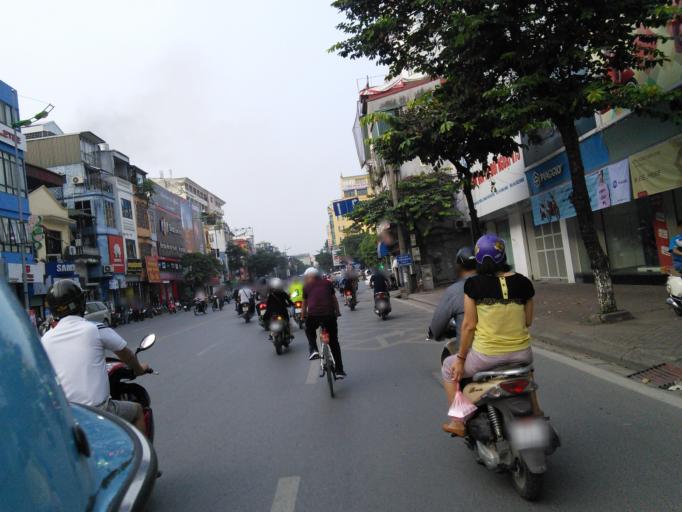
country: VN
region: Ha Noi
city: Hai BaTrung
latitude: 21.0169
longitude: 105.8414
